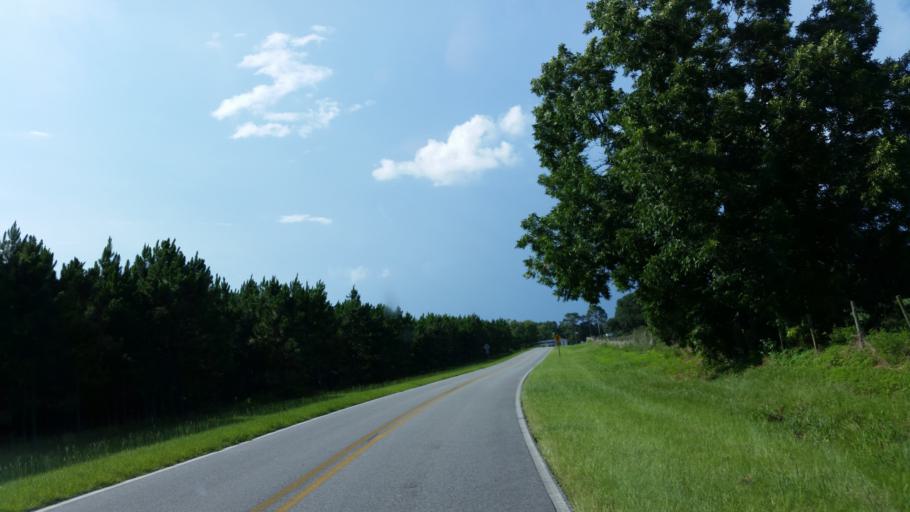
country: US
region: Georgia
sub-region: Lowndes County
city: Hahira
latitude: 30.9359
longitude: -83.4086
